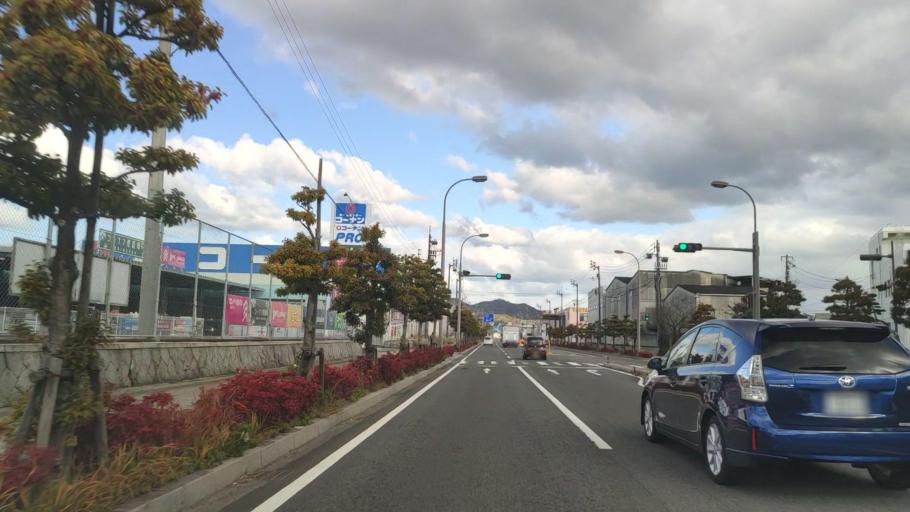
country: JP
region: Ehime
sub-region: Shikoku-chuo Shi
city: Matsuyama
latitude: 33.8510
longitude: 132.7132
